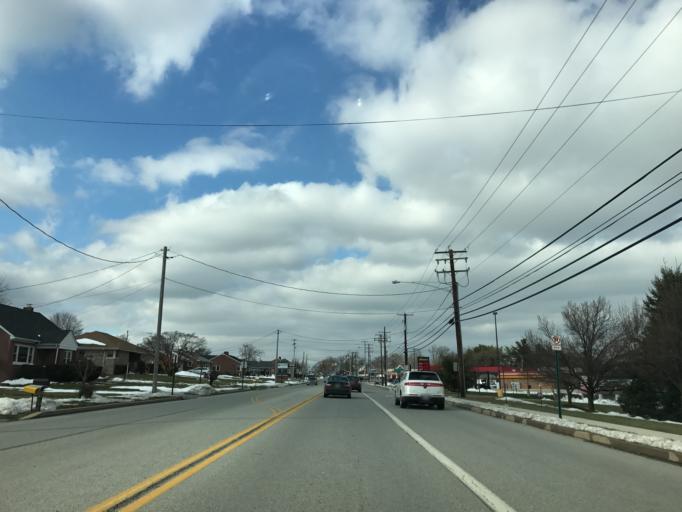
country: US
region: Pennsylvania
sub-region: York County
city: Parkville
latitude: 39.7722
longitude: -76.9604
